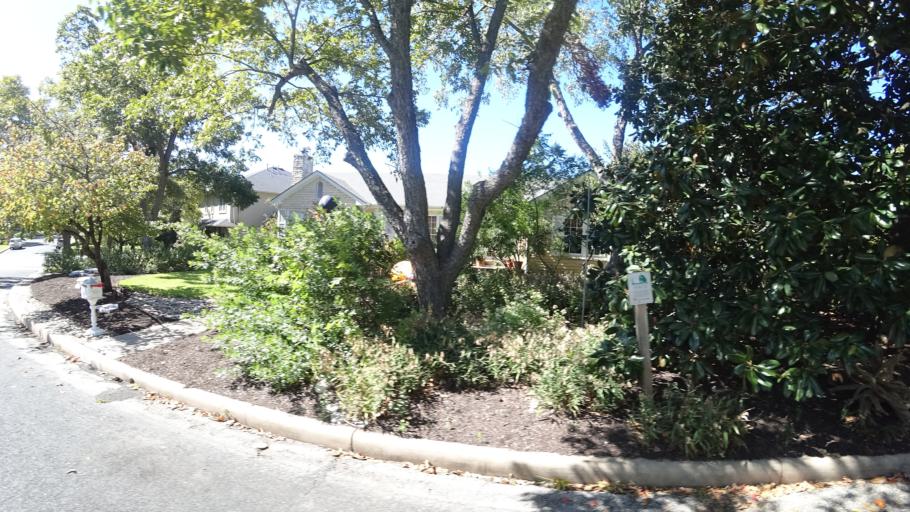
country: US
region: Texas
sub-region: Travis County
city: Rollingwood
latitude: 30.2972
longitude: -97.7644
